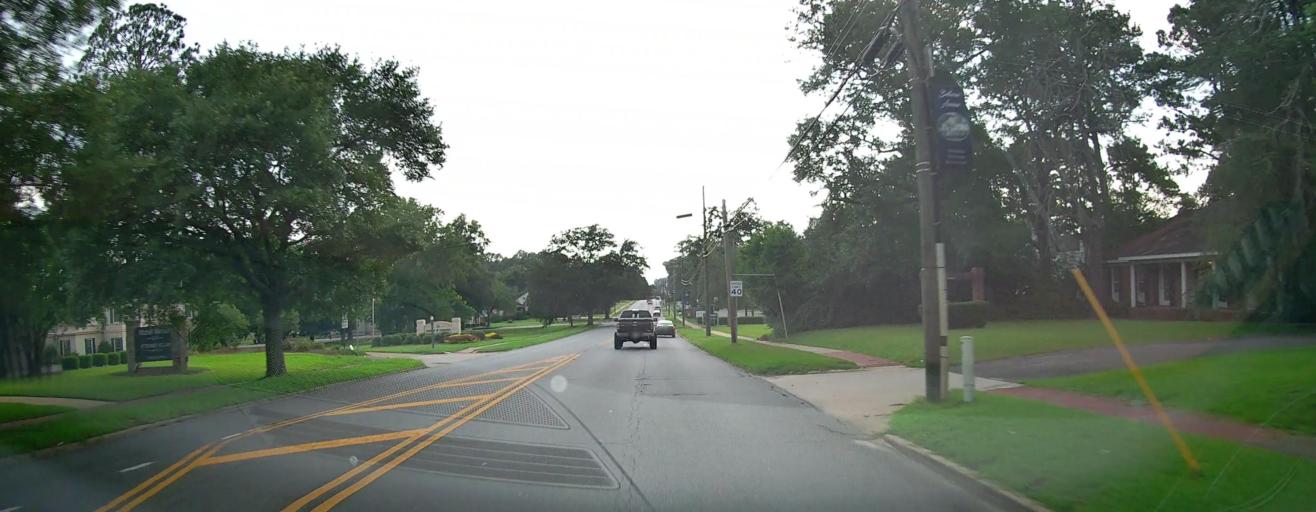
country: US
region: Georgia
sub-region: Laurens County
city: Dublin
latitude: 32.5365
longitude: -82.9207
